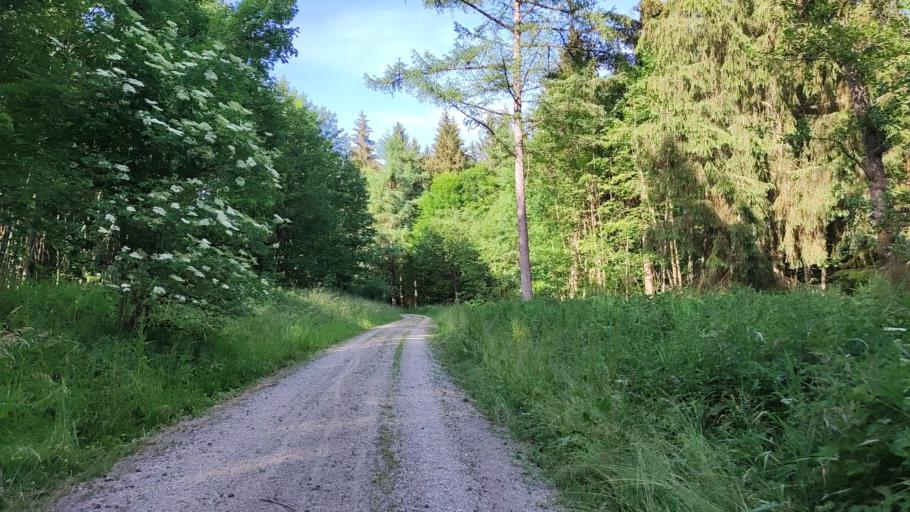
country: DE
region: Bavaria
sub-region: Swabia
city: Landensberg
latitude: 48.4187
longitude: 10.5043
